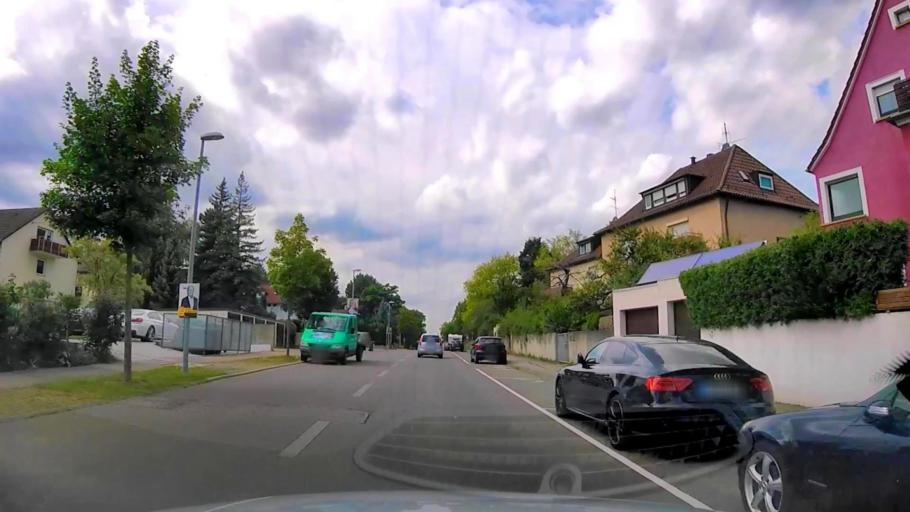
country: DE
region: Baden-Wuerttemberg
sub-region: Regierungsbezirk Stuttgart
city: Korntal
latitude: 48.8139
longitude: 9.1337
